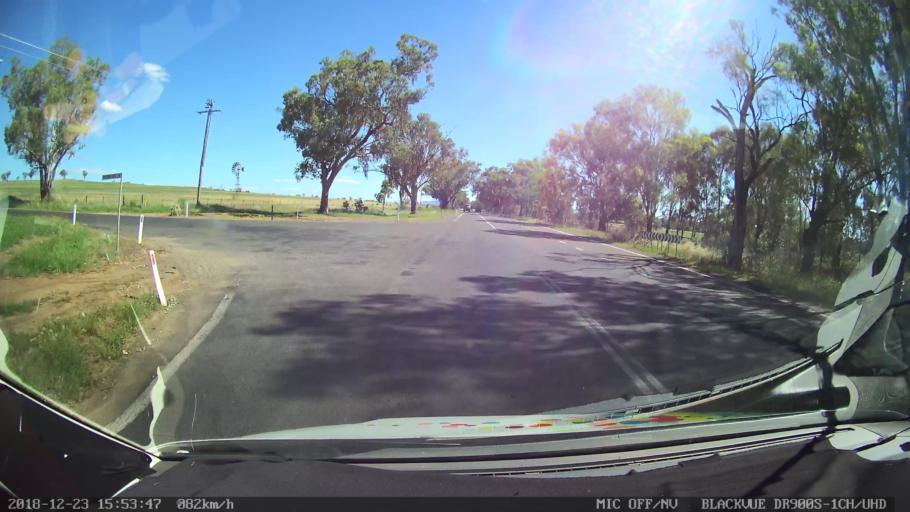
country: AU
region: New South Wales
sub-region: Tamworth Municipality
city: Phillip
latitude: -31.1376
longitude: 150.8792
